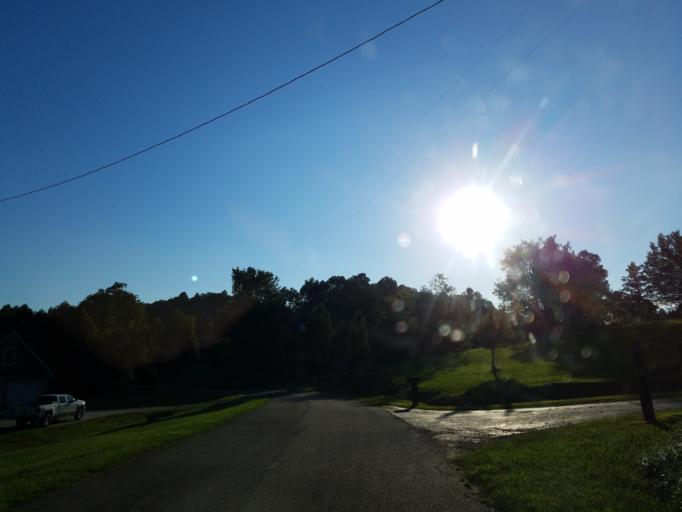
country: US
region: Georgia
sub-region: Lumpkin County
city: Dahlonega
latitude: 34.5827
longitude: -83.9804
